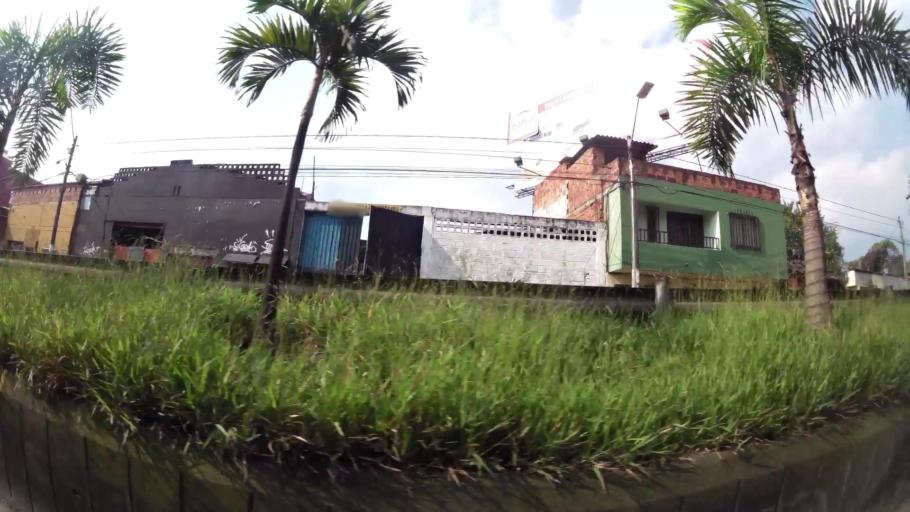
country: CO
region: Antioquia
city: Sabaneta
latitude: 6.1691
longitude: -75.6240
